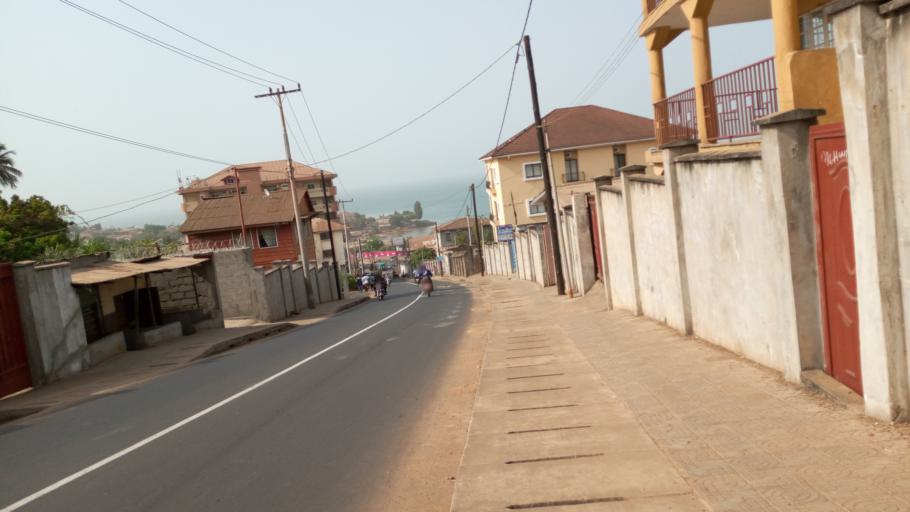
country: SL
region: Western Area
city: Freetown
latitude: 8.4813
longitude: -13.2587
